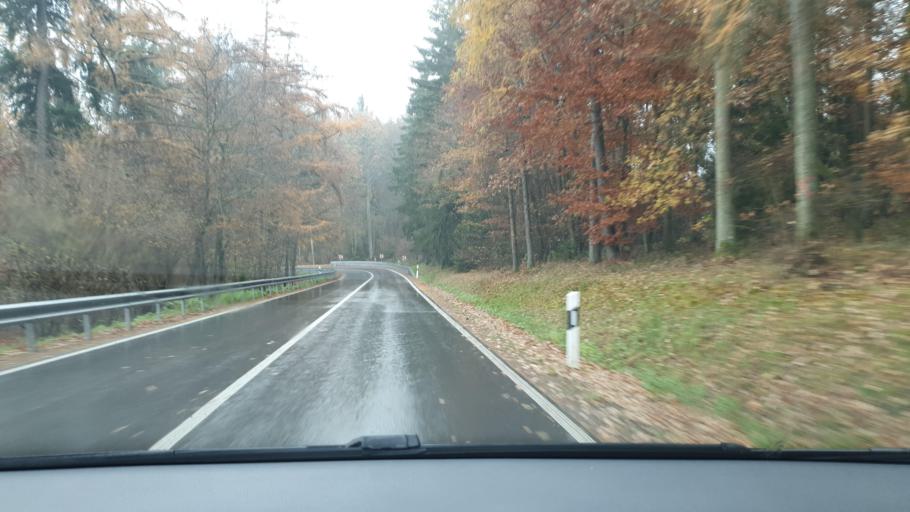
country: DE
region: Rheinland-Pfalz
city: Nieder Kostenz
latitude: 49.9364
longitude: 7.3808
